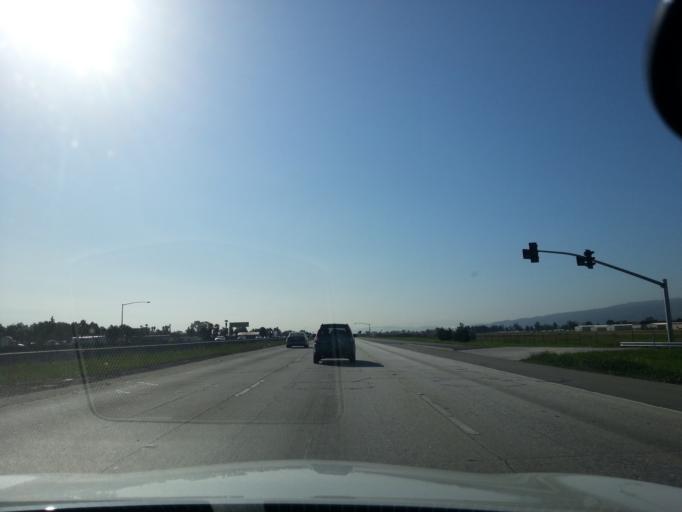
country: US
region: California
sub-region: Santa Clara County
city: San Martin
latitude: 37.0876
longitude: -121.5989
